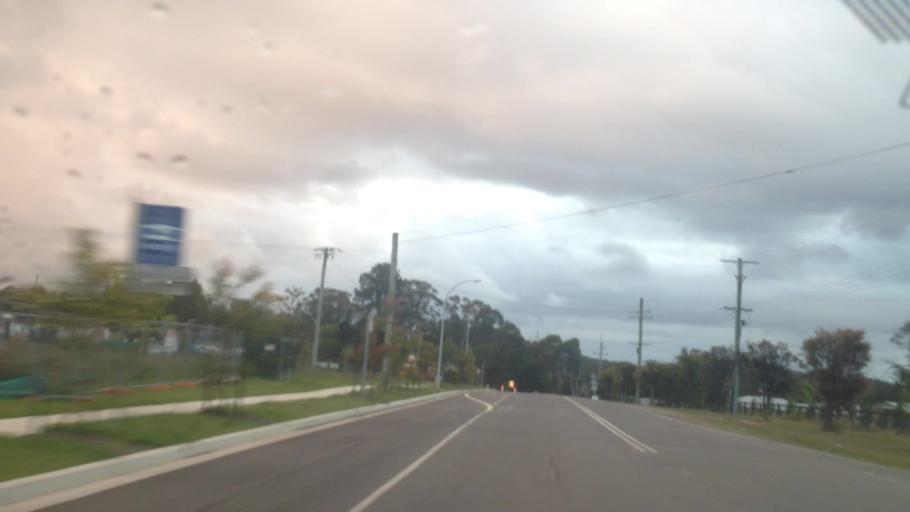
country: AU
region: New South Wales
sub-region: Lake Macquarie Shire
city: Dora Creek
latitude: -33.1051
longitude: 151.4770
